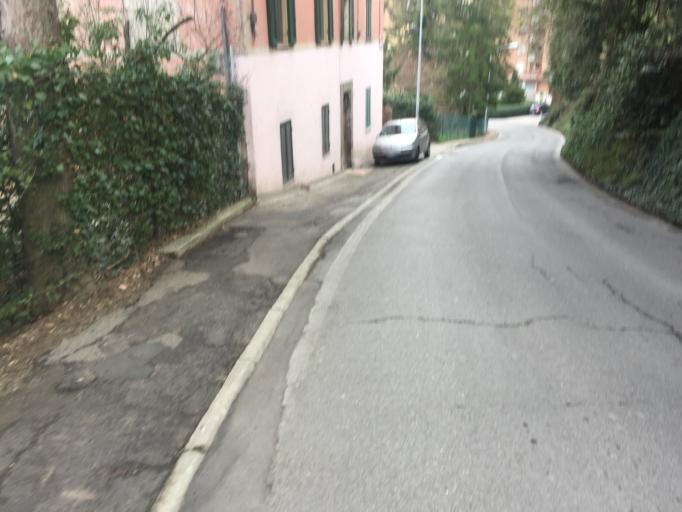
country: IT
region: Umbria
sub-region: Provincia di Perugia
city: Perugia
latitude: 43.1167
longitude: 12.3964
